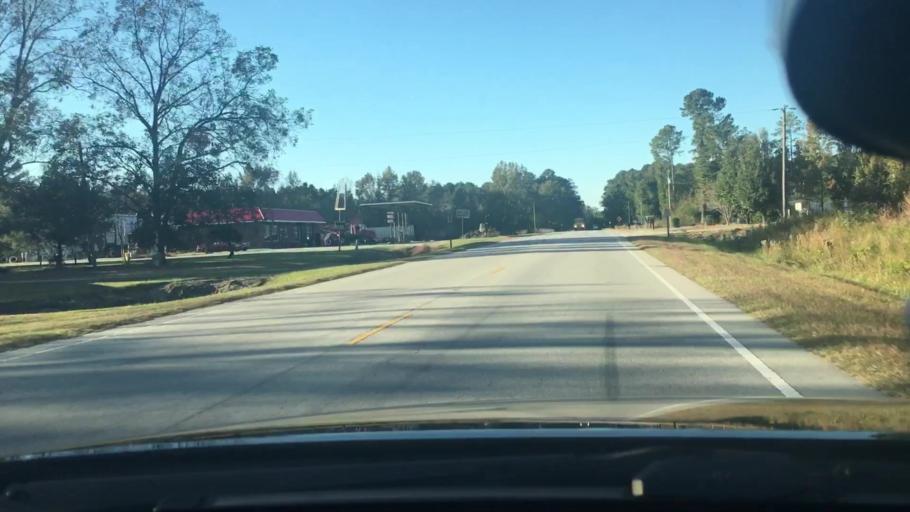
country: US
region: North Carolina
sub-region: Craven County
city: Vanceboro
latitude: 35.3161
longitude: -77.1423
